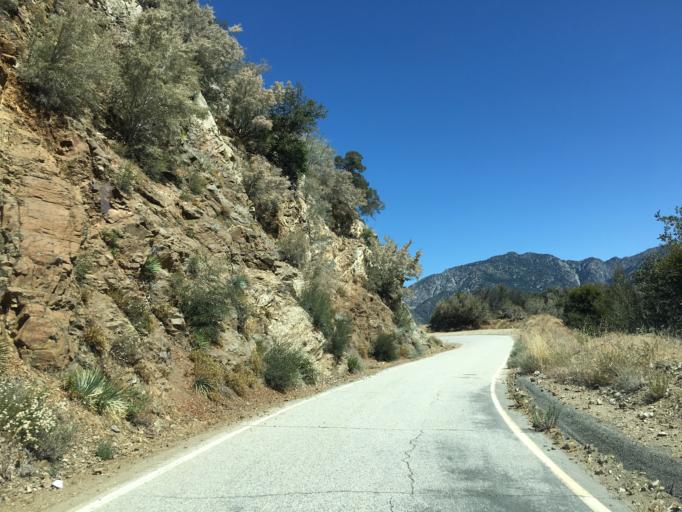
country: US
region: California
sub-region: San Bernardino County
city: San Antonio Heights
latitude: 34.2215
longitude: -117.7023
